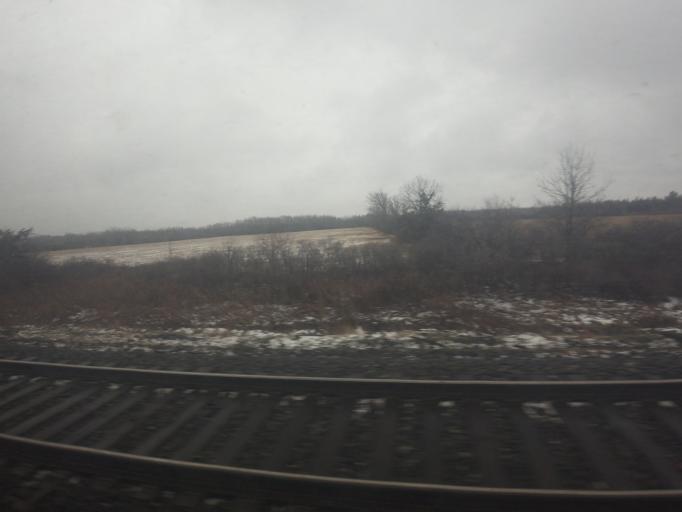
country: CA
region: Ontario
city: Deseronto
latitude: 44.2171
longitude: -77.1643
